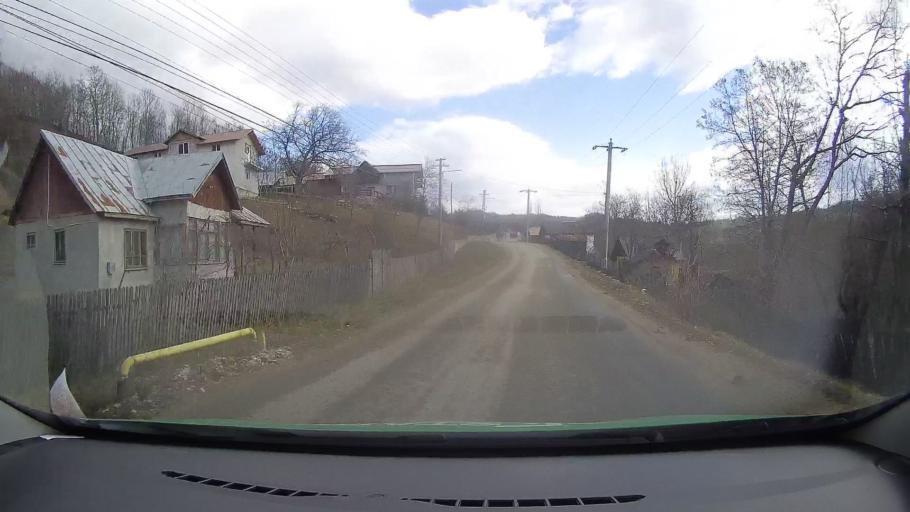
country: RO
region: Dambovita
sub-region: Comuna Buciumeni
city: Buciumeni
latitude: 45.1213
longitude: 25.4605
